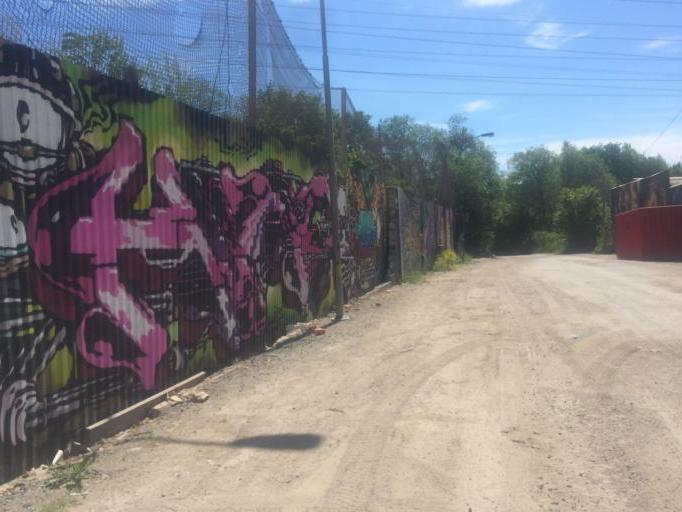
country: SE
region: Stockholm
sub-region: Stockholms Kommun
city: Arsta
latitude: 59.2495
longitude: 18.0419
